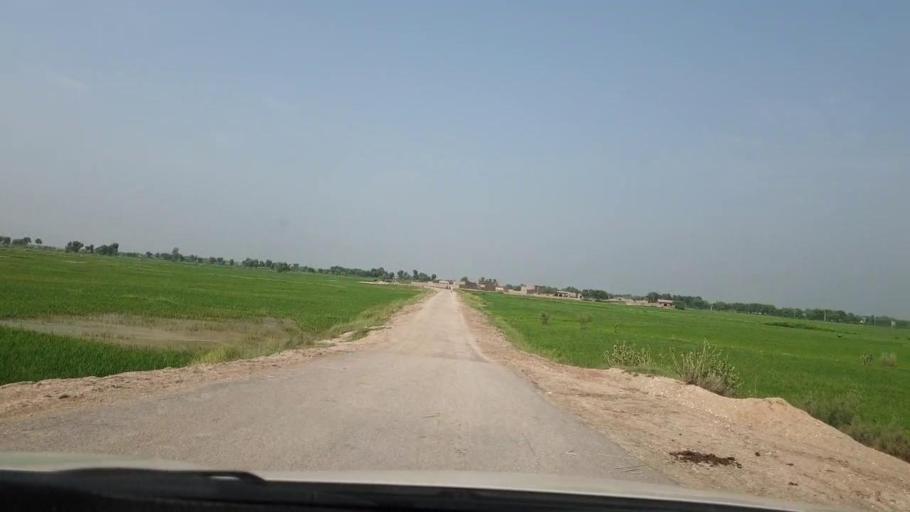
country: PK
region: Sindh
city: Larkana
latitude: 27.4369
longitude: 68.2580
